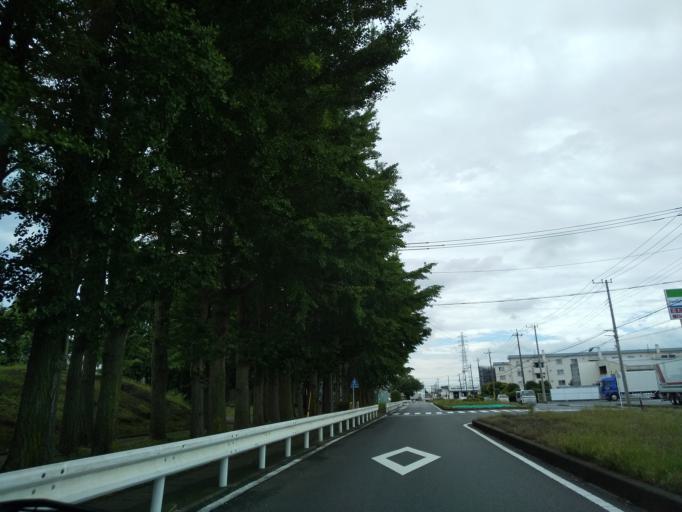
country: JP
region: Kanagawa
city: Zama
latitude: 35.5098
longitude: 139.3448
